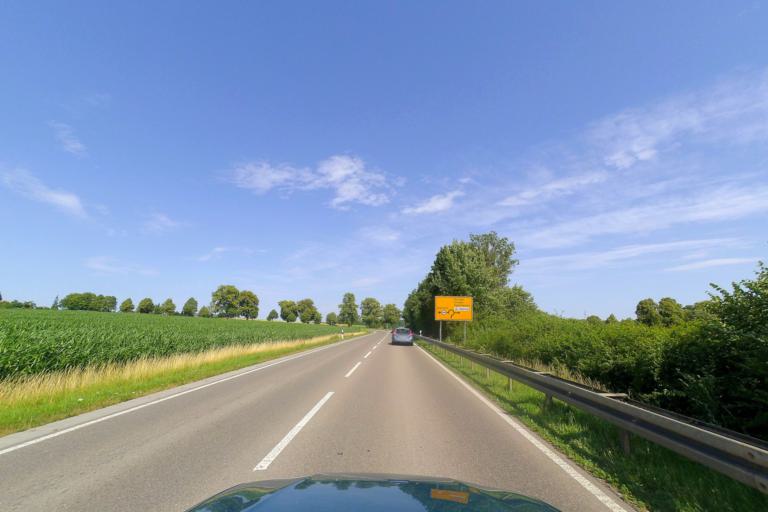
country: DE
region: Baden-Wuerttemberg
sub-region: Regierungsbezirk Stuttgart
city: Nattheim
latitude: 48.6927
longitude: 10.2328
